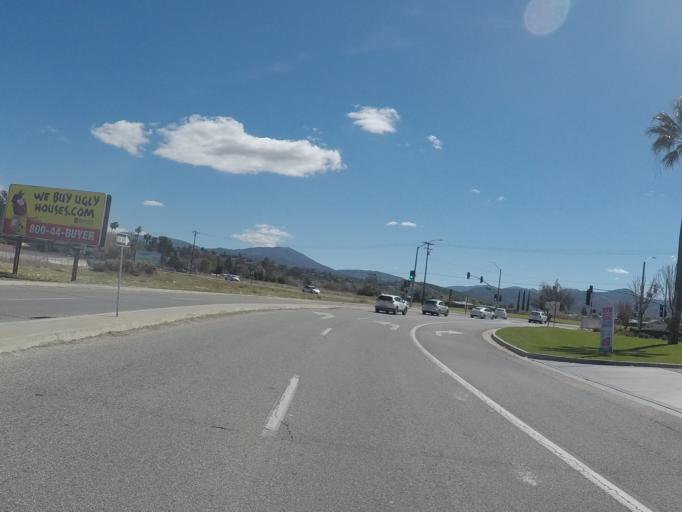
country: US
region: California
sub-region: Riverside County
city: Valle Vista
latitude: 33.7486
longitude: -116.9012
